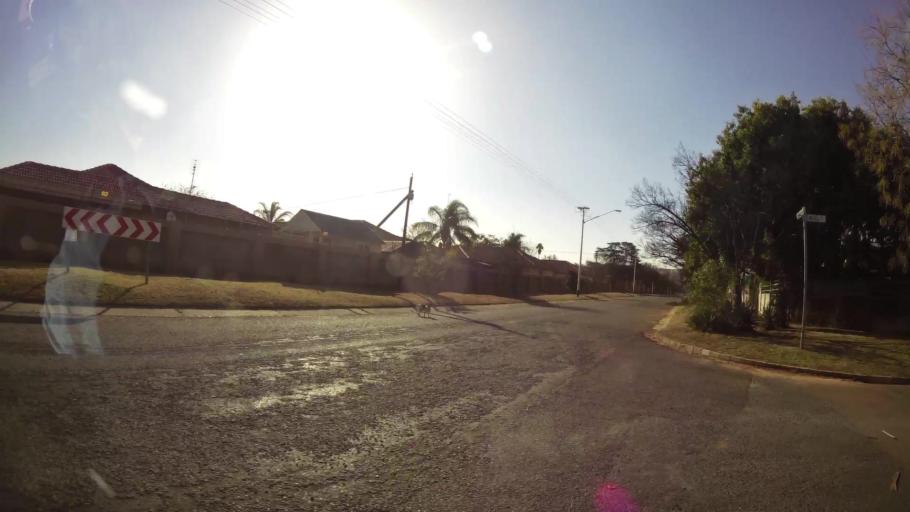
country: ZA
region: Gauteng
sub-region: City of Tshwane Metropolitan Municipality
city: Pretoria
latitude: -25.7141
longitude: 28.2453
